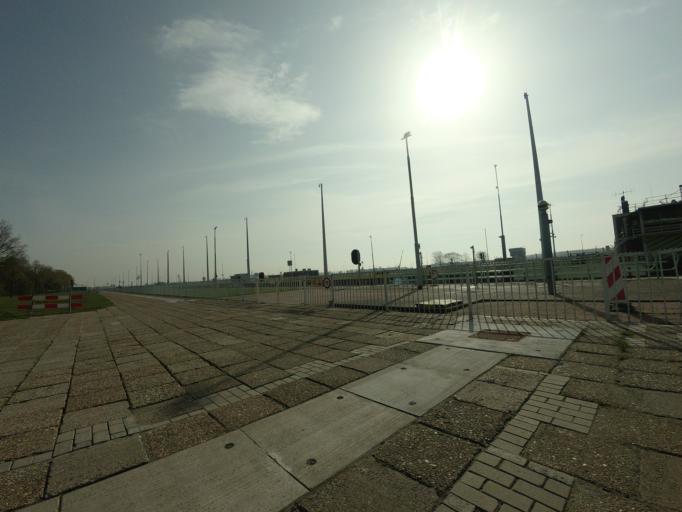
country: NL
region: Zeeland
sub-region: Gemeente Terneuzen
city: Terneuzen
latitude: 51.3359
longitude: 3.8202
